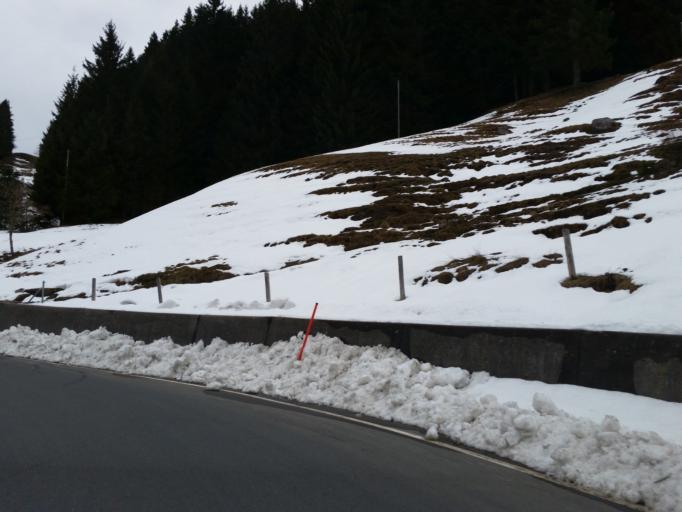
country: CH
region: Appenzell Ausserrhoden
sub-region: Bezirk Hinterland
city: Urnasch
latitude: 47.2631
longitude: 9.2991
